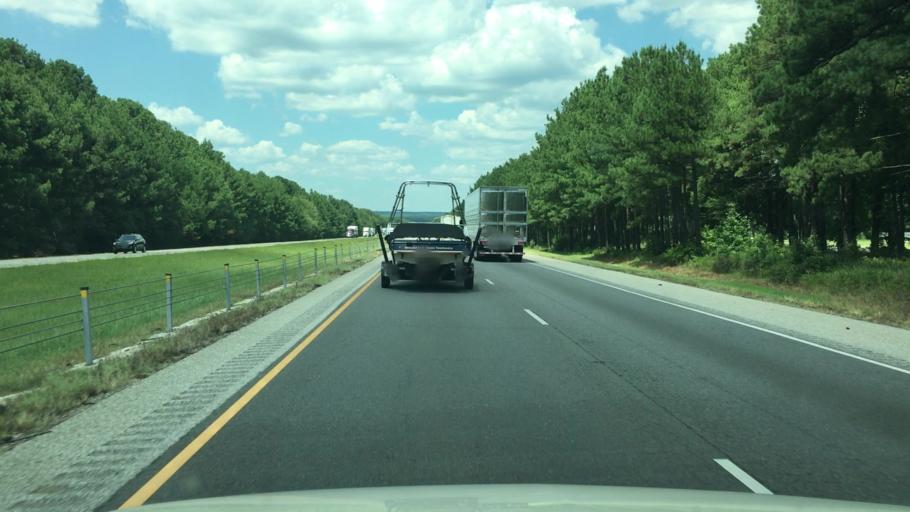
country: US
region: Arkansas
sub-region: Clark County
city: Arkadelphia
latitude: 34.1498
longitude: -93.0786
